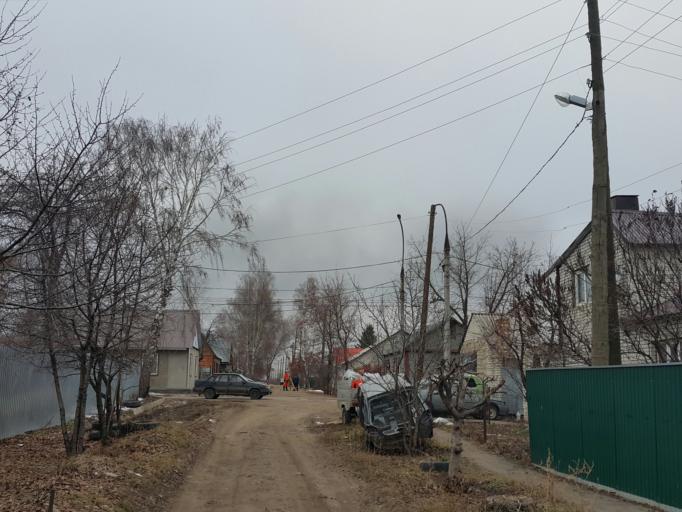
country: RU
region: Tambov
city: Tambov
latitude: 52.7242
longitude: 41.4019
